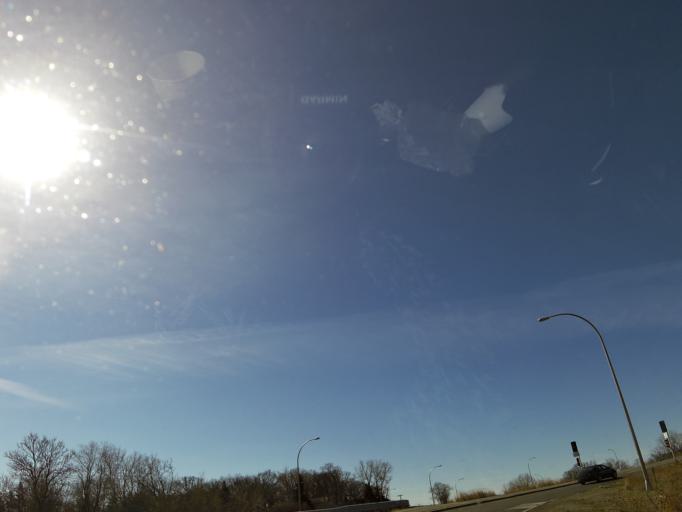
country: US
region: Minnesota
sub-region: Hennepin County
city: Edina
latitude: 44.8899
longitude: -93.3977
